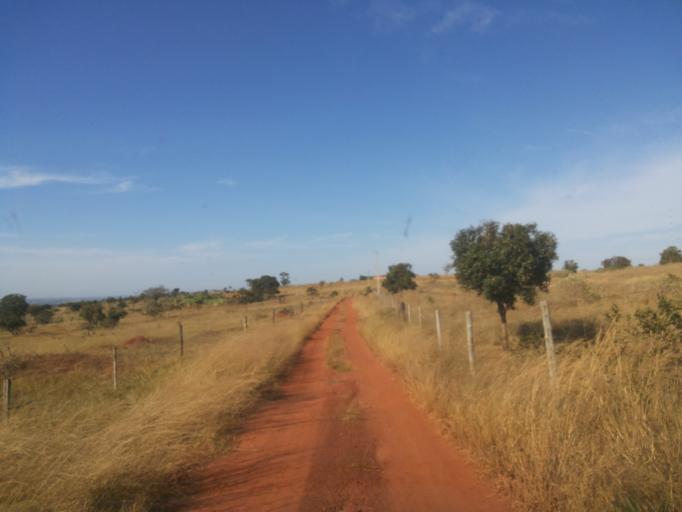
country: BR
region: Minas Gerais
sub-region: Ituiutaba
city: Ituiutaba
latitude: -19.1245
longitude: -49.3959
